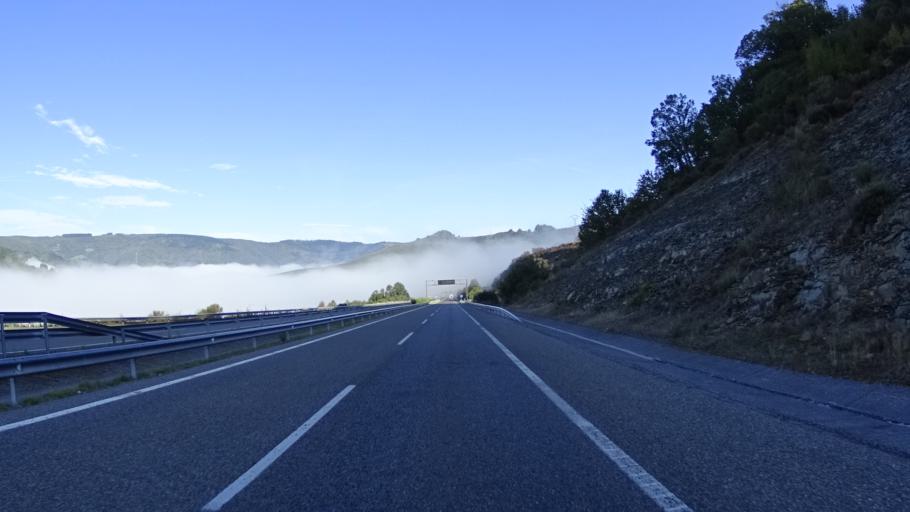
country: ES
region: Galicia
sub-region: Provincia de Lugo
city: San Roman
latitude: 42.7757
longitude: -7.0964
